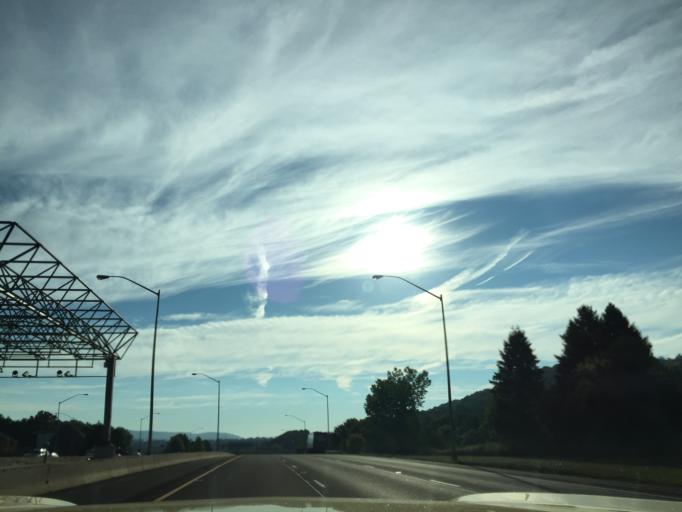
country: US
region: New Jersey
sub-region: Warren County
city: Phillipsburg
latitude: 40.6745
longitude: -75.2014
